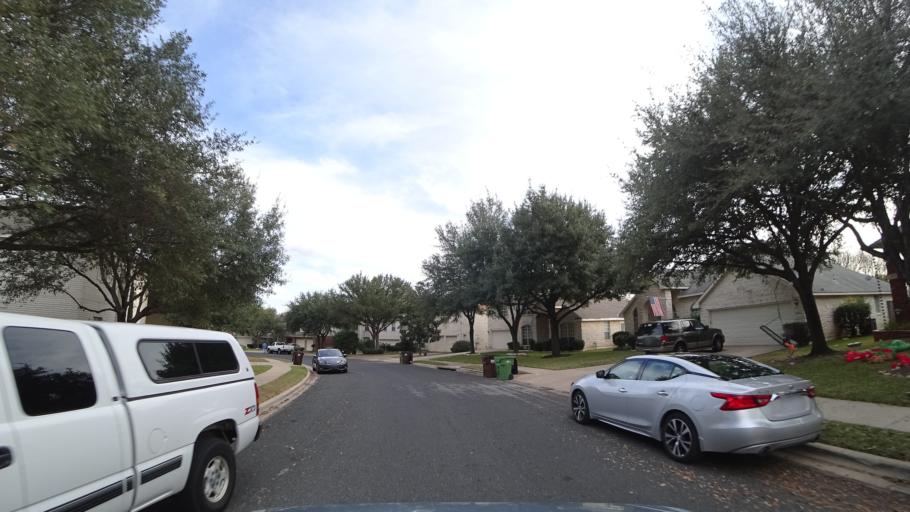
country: US
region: Texas
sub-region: Williamson County
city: Brushy Creek
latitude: 30.5126
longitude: -97.7254
